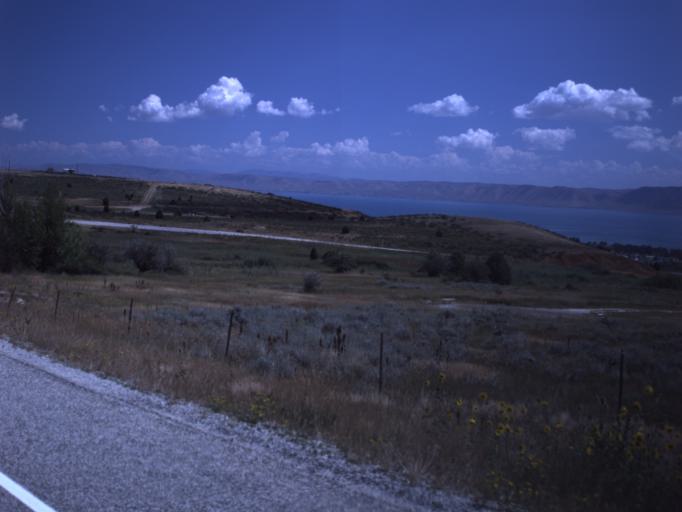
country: US
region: Idaho
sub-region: Bear Lake County
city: Paris
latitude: 41.9278
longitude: -111.4259
